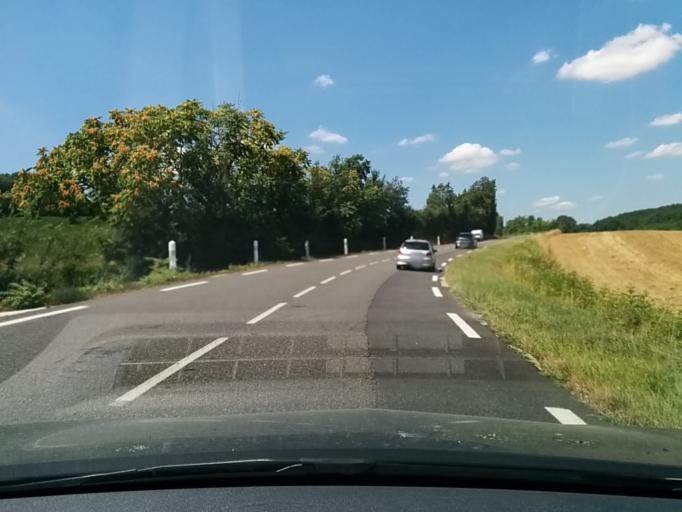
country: FR
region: Midi-Pyrenees
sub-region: Departement du Gers
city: Vic-Fezensac
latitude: 43.7438
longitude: 0.3509
